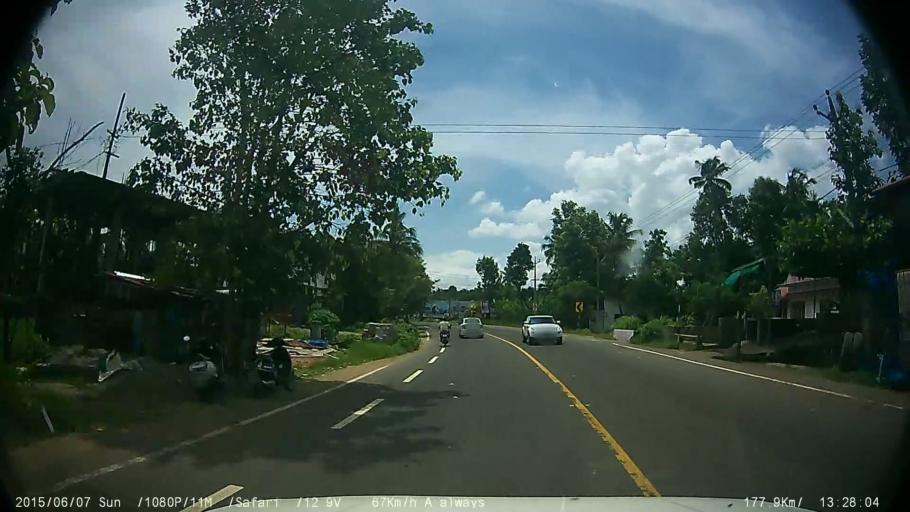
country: IN
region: Kerala
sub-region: Ernakulam
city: Muvattupula
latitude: 10.0233
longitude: 76.5576
